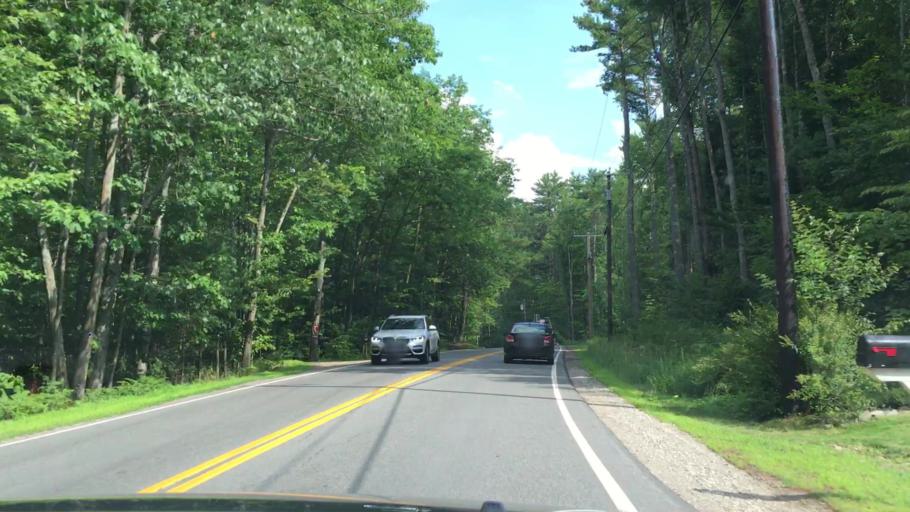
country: US
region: New Hampshire
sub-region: Belknap County
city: Gilford
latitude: 43.5846
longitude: -71.4150
